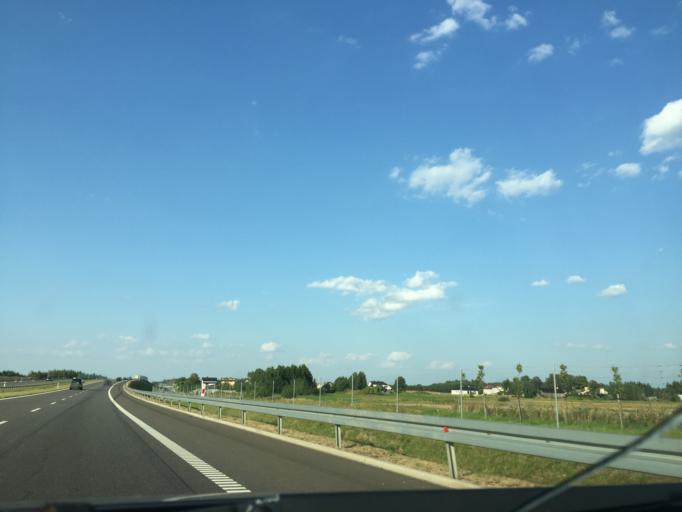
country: PL
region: Masovian Voivodeship
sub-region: Powiat radomski
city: Zakrzew
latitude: 51.4692
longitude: 21.0512
